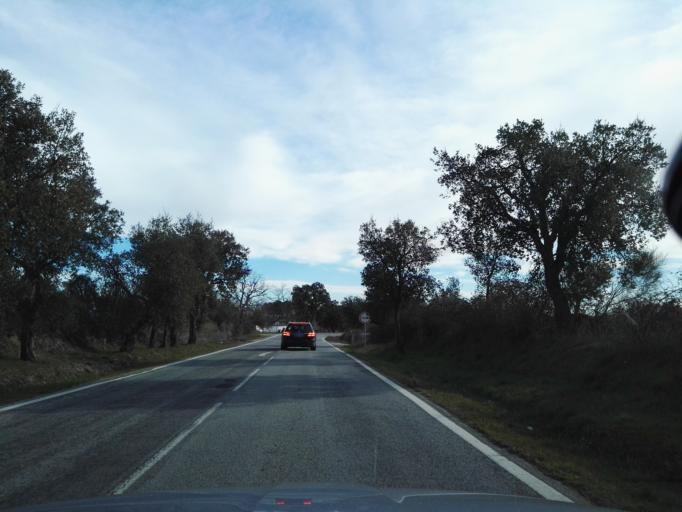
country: PT
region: Portalegre
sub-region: Nisa
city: Nisa
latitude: 39.4980
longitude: -7.7006
